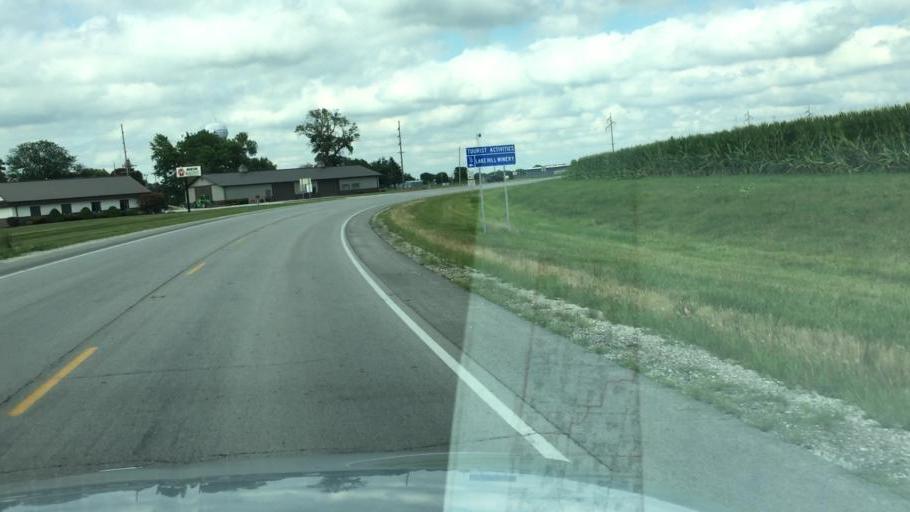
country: US
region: Illinois
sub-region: Hancock County
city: Carthage
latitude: 40.4150
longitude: -91.1546
